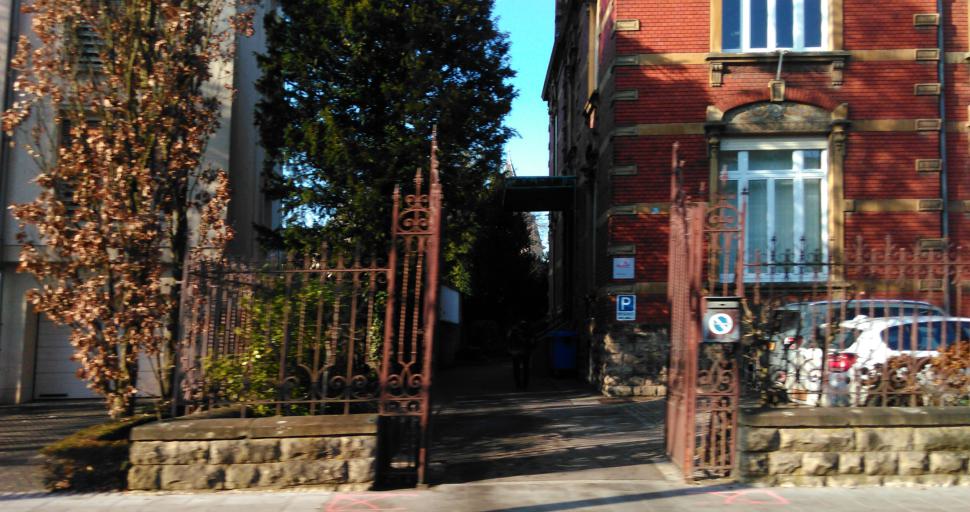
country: LU
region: Luxembourg
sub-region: Canton de Luxembourg
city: Luxembourg
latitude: 49.6119
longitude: 6.1202
